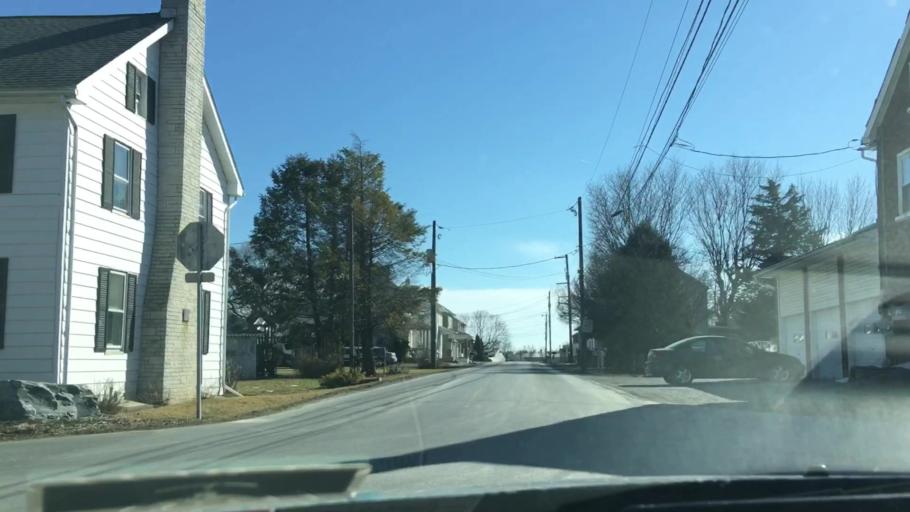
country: US
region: Pennsylvania
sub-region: Lancaster County
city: New Holland
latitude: 40.1245
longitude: -76.1301
